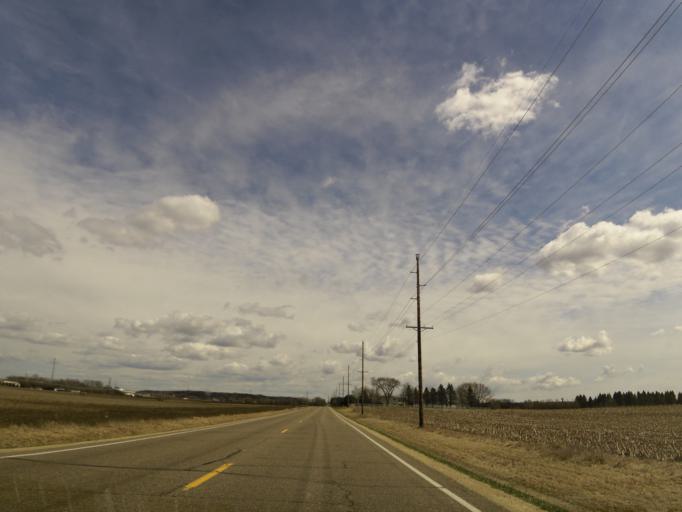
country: US
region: Minnesota
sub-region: Goodhue County
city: Cannon Falls
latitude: 44.5217
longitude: -92.9535
